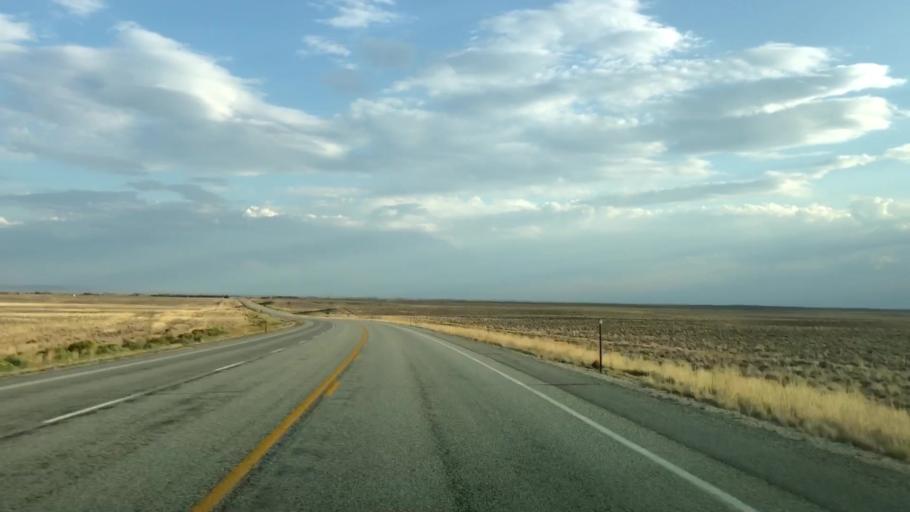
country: US
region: Wyoming
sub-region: Sweetwater County
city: North Rock Springs
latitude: 42.1910
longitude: -109.4807
